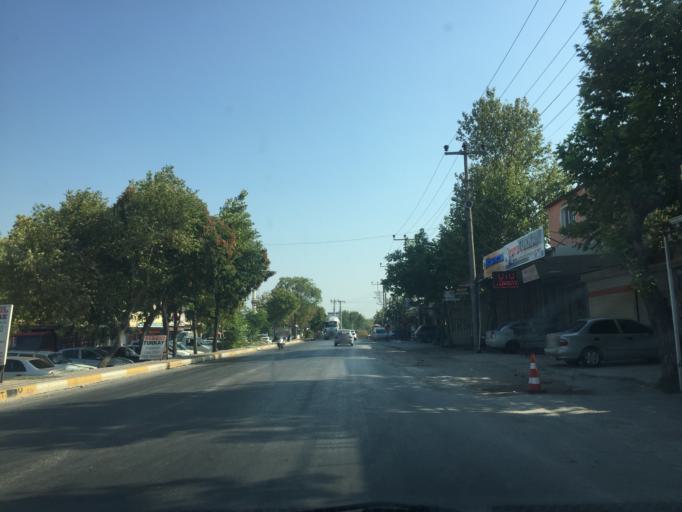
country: TR
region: Manisa
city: Akhisar
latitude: 38.9089
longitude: 27.8370
